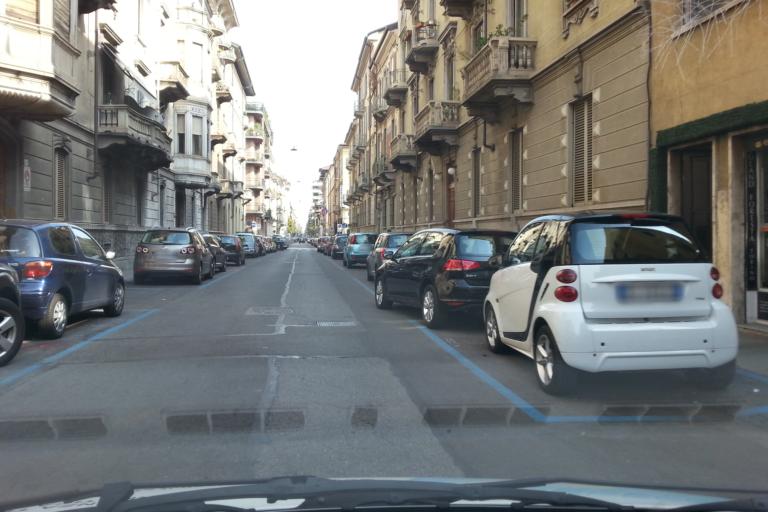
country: IT
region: Piedmont
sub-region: Provincia di Torino
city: Turin
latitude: 45.0529
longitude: 7.6811
